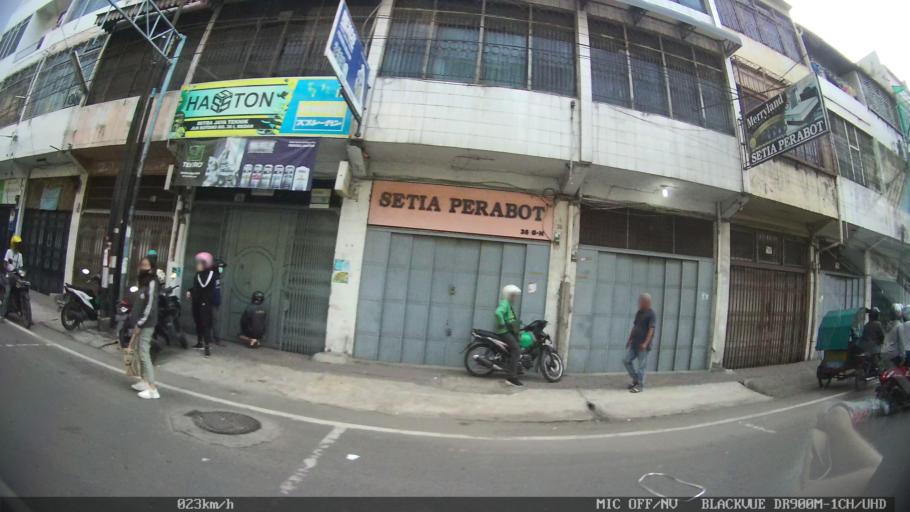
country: ID
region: North Sumatra
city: Medan
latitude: 3.5847
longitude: 98.6867
